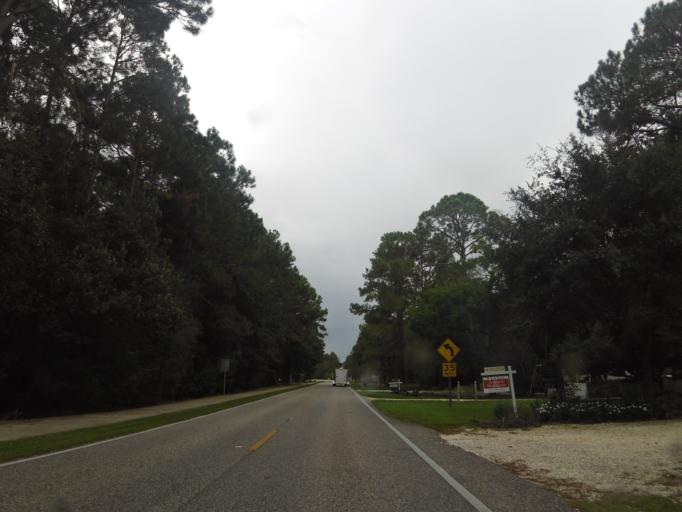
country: US
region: Alabama
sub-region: Baldwin County
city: Point Clear
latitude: 30.4254
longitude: -87.9095
